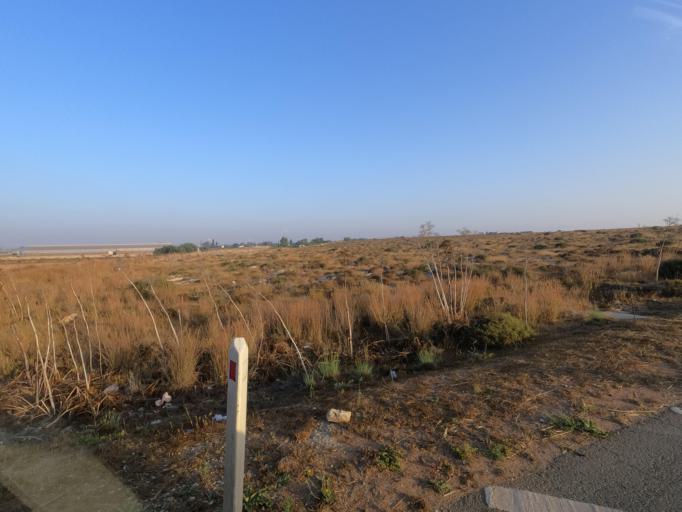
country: CY
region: Ammochostos
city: Frenaros
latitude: 35.0052
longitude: 33.9371
